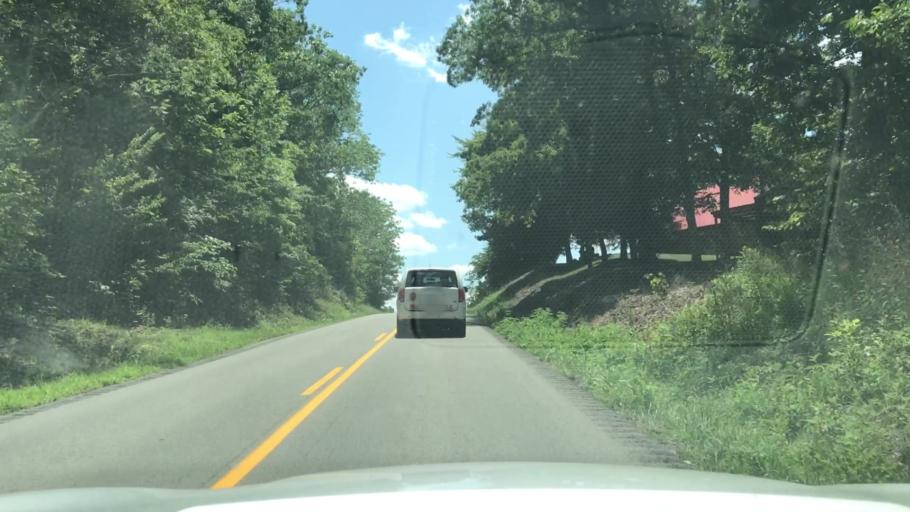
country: US
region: Kentucky
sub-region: Christian County
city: Hopkinsville
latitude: 36.9060
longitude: -87.4460
